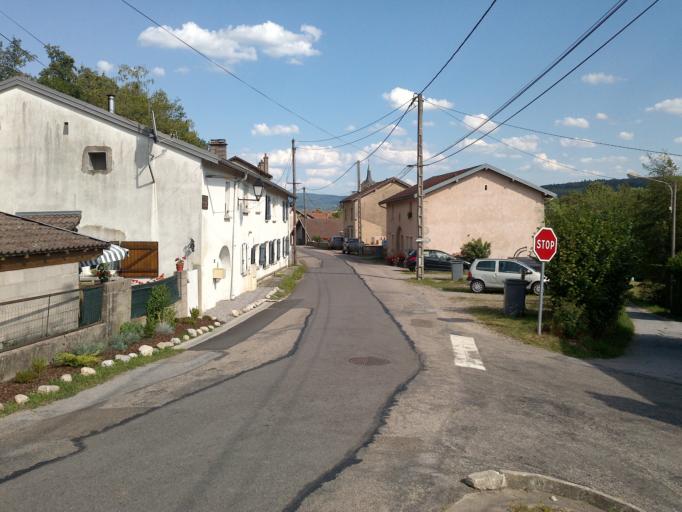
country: FR
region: Lorraine
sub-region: Departement des Vosges
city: Arches
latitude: 48.1250
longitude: 6.5284
